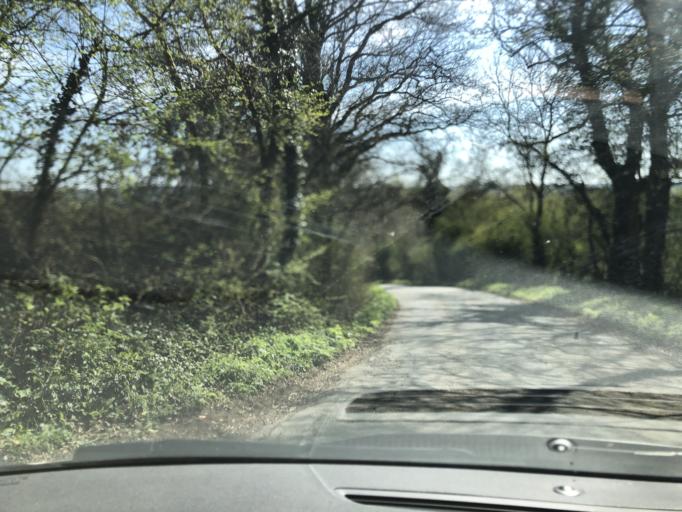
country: GB
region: England
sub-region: Oxfordshire
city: Hook Norton
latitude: 52.0078
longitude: -1.4403
